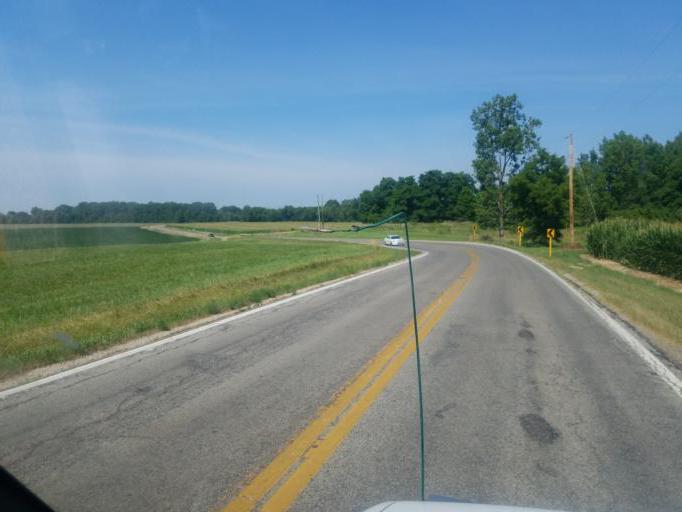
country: US
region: Ohio
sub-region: Champaign County
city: North Lewisburg
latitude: 40.2302
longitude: -83.5127
